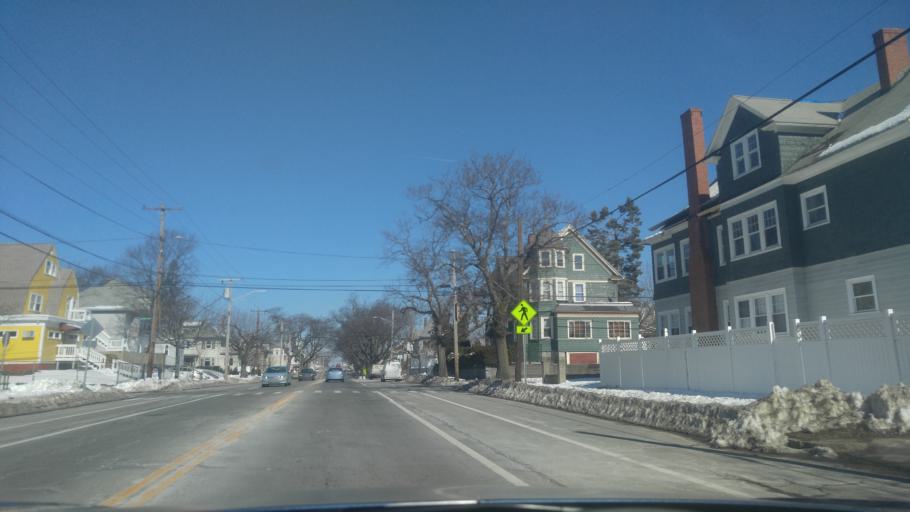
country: US
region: Rhode Island
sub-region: Providence County
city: East Providence
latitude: 41.7872
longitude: -71.3953
